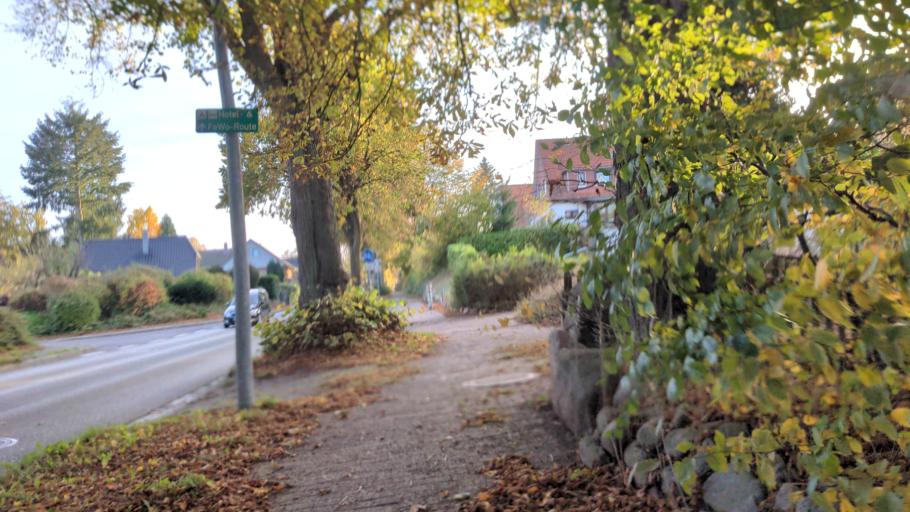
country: DE
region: Schleswig-Holstein
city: Eutin
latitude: 54.1585
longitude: 10.6108
